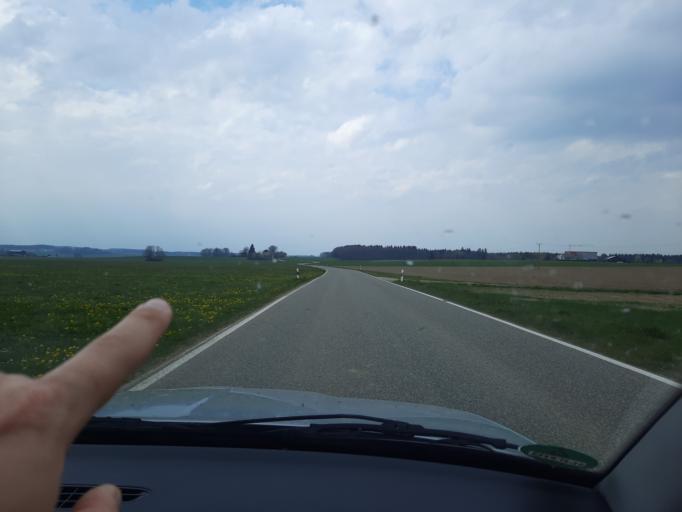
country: DE
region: Baden-Wuerttemberg
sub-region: Tuebingen Region
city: Steinhausen an der Rottum
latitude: 47.9563
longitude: 9.9687
